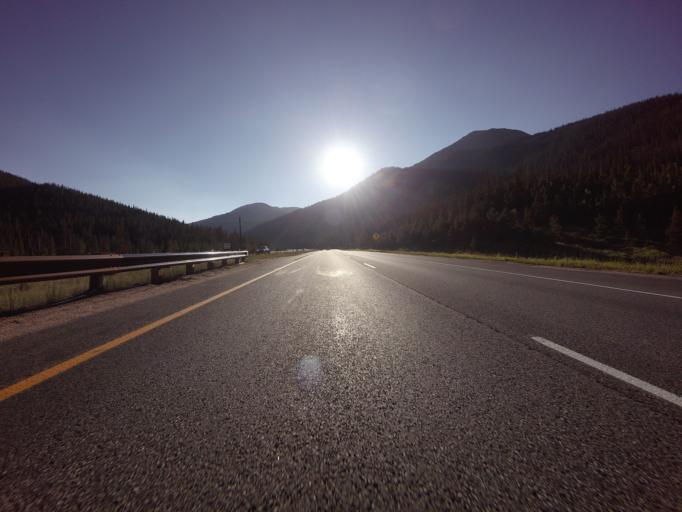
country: US
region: Colorado
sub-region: Summit County
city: Keystone
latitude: 39.7016
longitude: -105.8610
